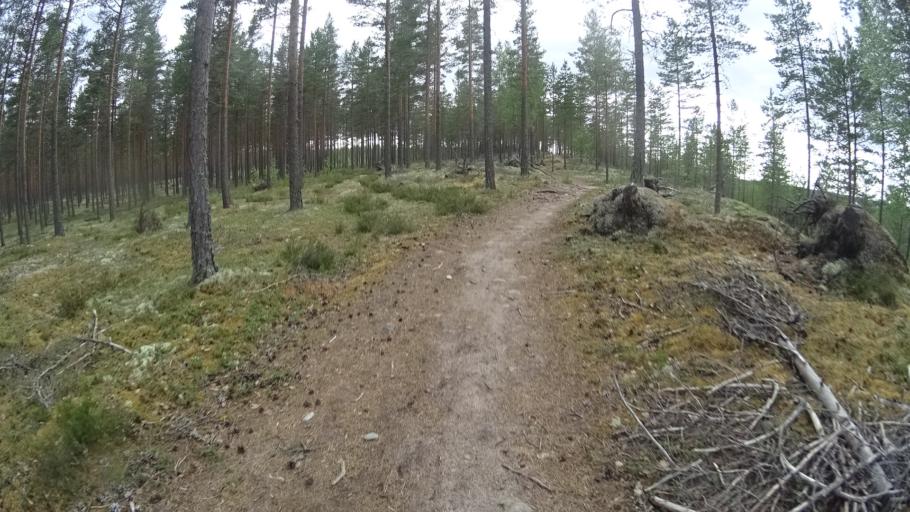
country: FI
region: Satakunta
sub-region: Pohjois-Satakunta
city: Jaemijaervi
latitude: 61.7714
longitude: 22.8014
